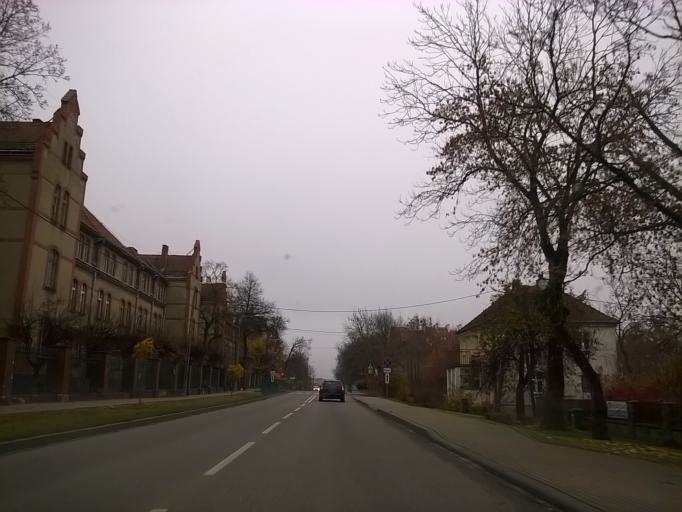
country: PL
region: Warmian-Masurian Voivodeship
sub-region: Powiat ketrzynski
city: Ketrzyn
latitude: 54.0844
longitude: 21.3520
